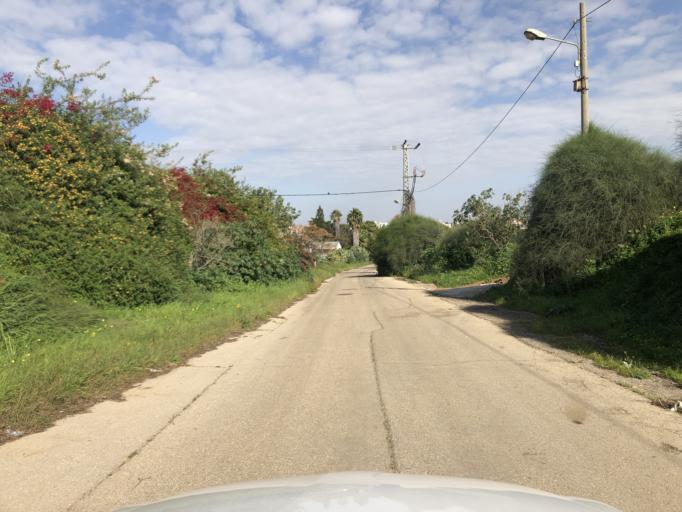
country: IL
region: Central District
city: Ness Ziona
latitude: 31.9160
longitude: 34.7962
